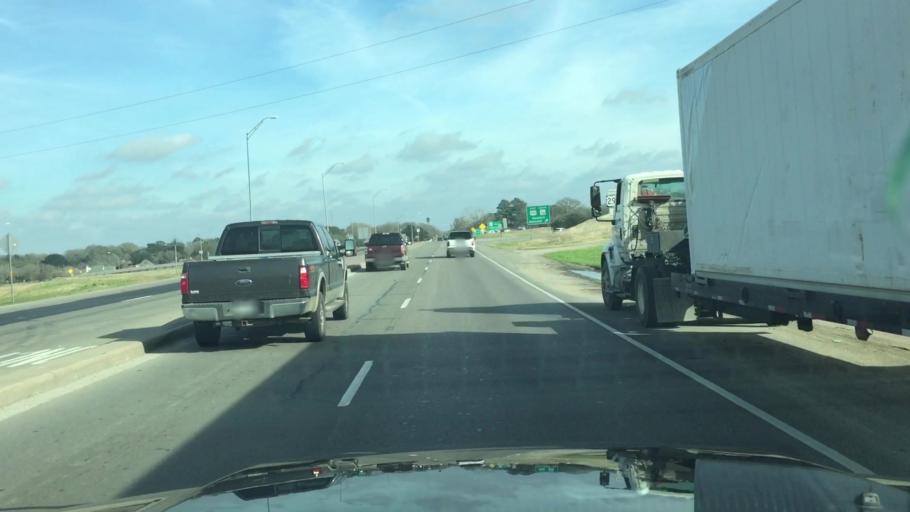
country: US
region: Texas
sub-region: Washington County
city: Brenham
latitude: 30.1663
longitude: -96.4274
